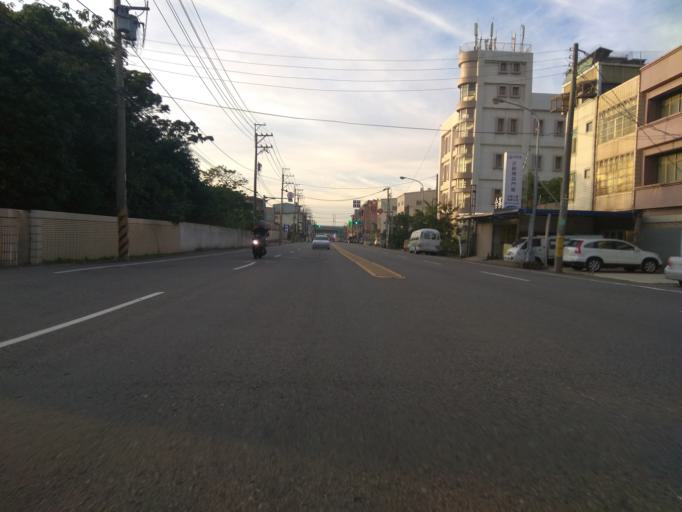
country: TW
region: Taiwan
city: Taoyuan City
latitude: 24.9830
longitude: 121.1898
